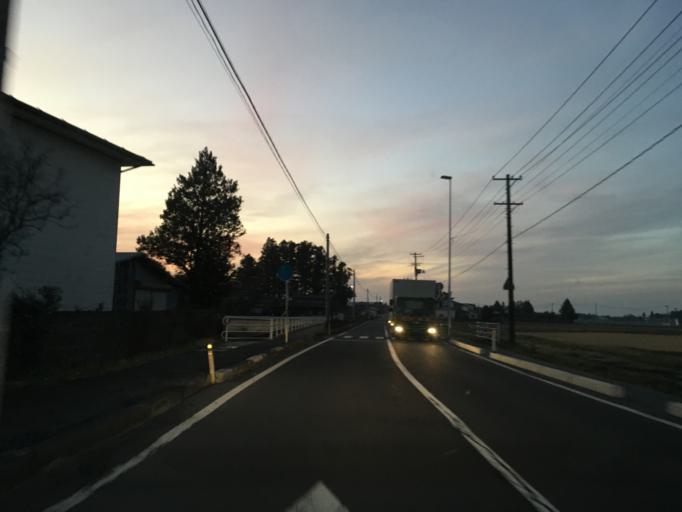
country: JP
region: Miyagi
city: Wakuya
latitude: 38.7127
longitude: 141.2248
